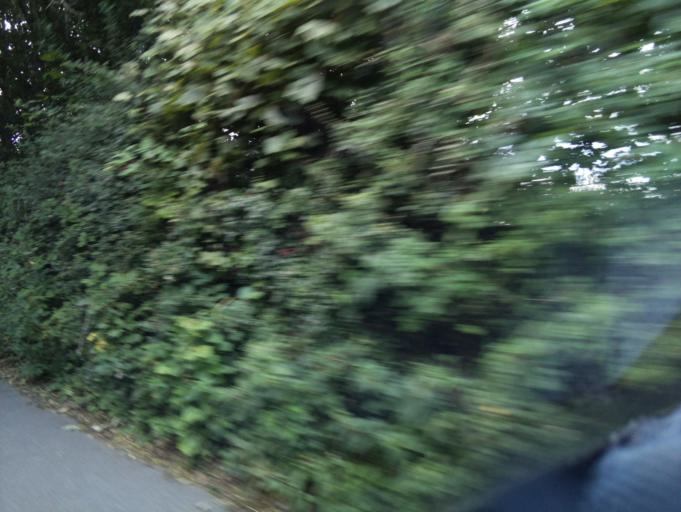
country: GB
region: England
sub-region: Devon
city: Buckfastleigh
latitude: 50.5334
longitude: -3.8275
